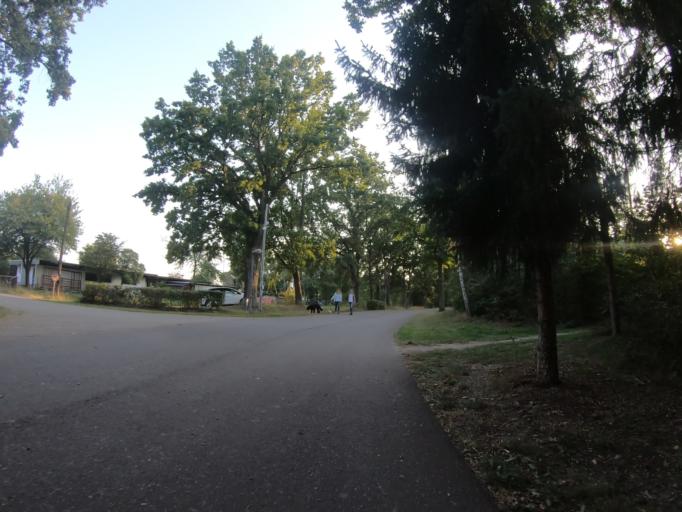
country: DE
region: Lower Saxony
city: Calberlah
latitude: 52.4511
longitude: 10.6158
